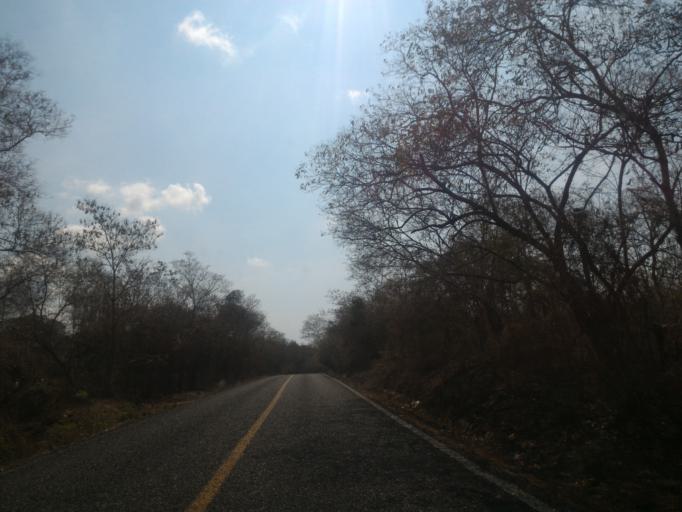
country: MX
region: Michoacan
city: Coahuayana Viejo
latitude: 18.3837
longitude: -103.5200
